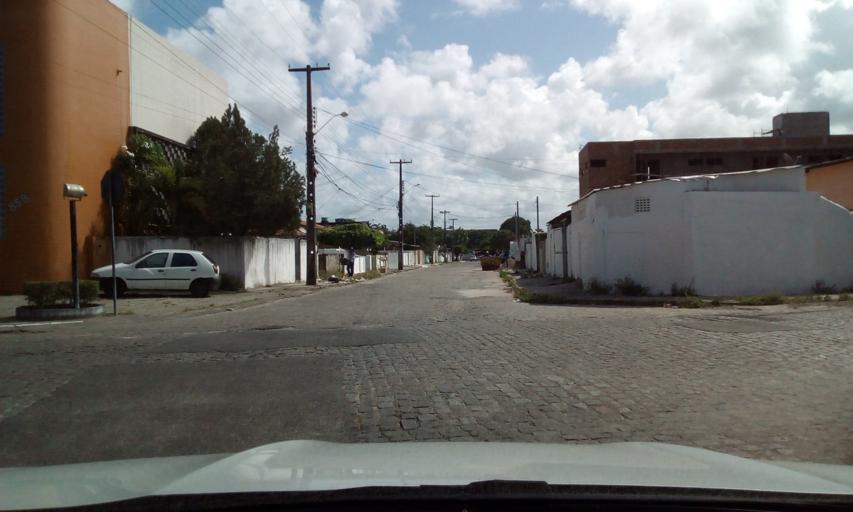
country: BR
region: Paraiba
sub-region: Joao Pessoa
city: Joao Pessoa
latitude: -7.1325
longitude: -34.8727
